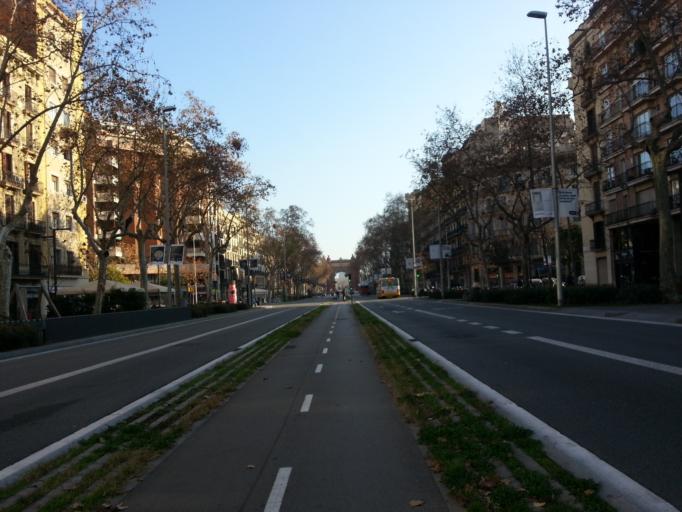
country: ES
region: Catalonia
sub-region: Provincia de Barcelona
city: Ciutat Vella
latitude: 41.3936
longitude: 2.1772
